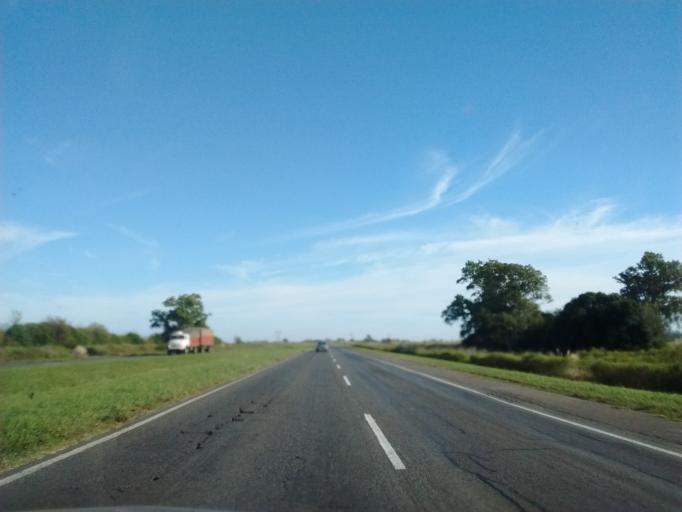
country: AR
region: Santa Fe
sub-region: Departamento de San Lorenzo
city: San Lorenzo
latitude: -32.6010
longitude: -60.8543
